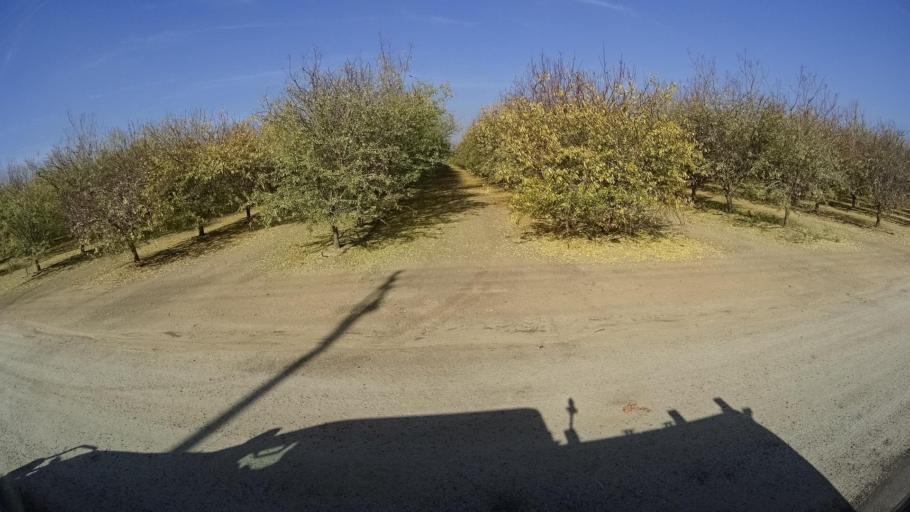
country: US
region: California
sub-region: Kern County
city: McFarland
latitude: 35.6311
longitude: -119.1786
